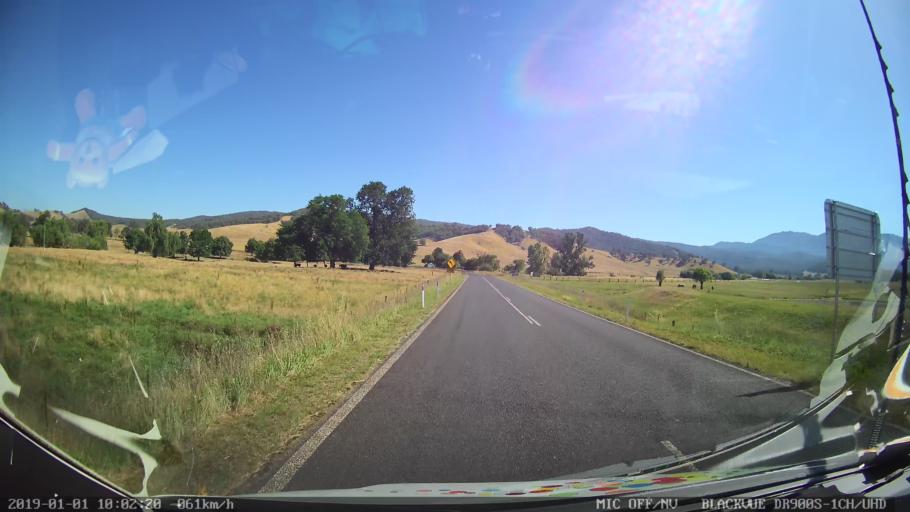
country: AU
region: New South Wales
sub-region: Snowy River
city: Jindabyne
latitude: -36.1823
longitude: 148.1019
